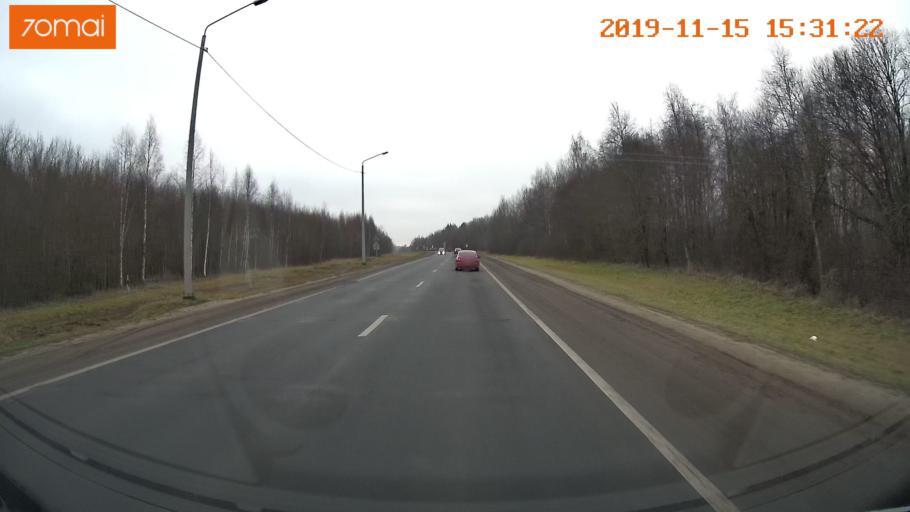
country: RU
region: Jaroslavl
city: Danilov
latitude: 58.1010
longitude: 40.1078
